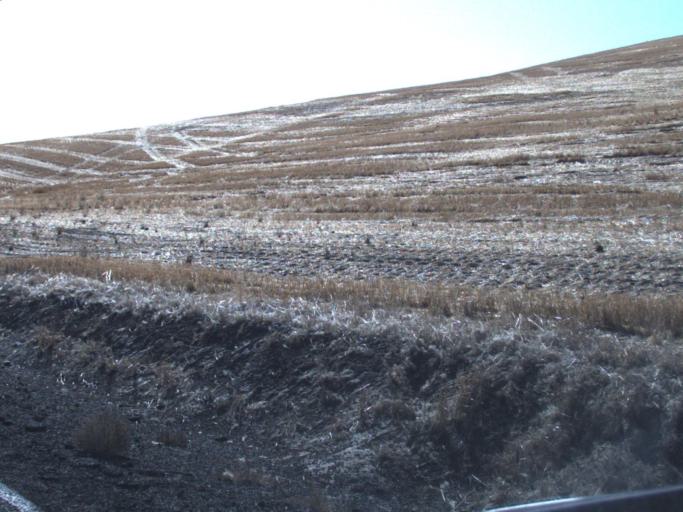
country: US
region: Washington
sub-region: Walla Walla County
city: Walla Walla
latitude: 46.1900
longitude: -118.3836
